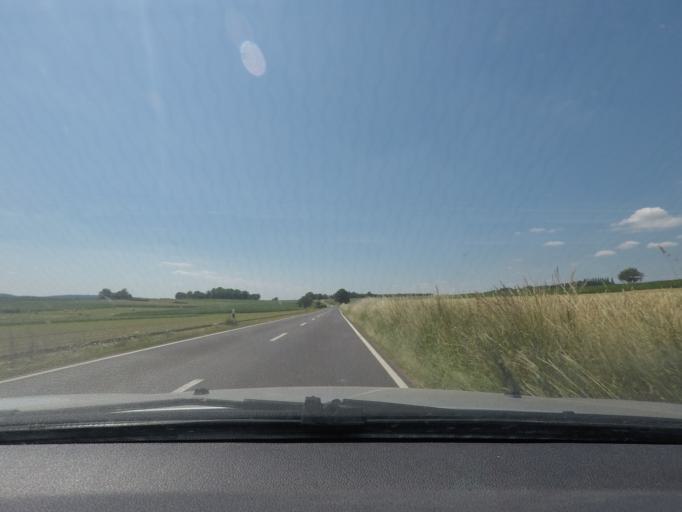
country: LU
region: Diekirch
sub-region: Canton de Redange
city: Ell
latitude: 49.7605
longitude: 5.8407
